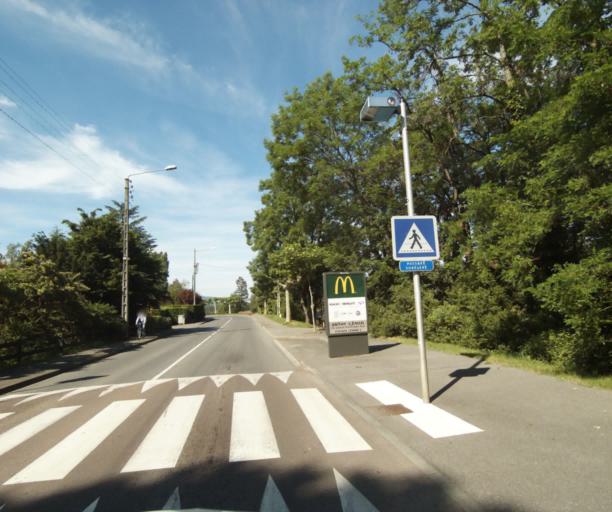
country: FR
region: Rhone-Alpes
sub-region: Departement de la Haute-Savoie
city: Thonon-les-Bains
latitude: 46.3665
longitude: 6.4567
